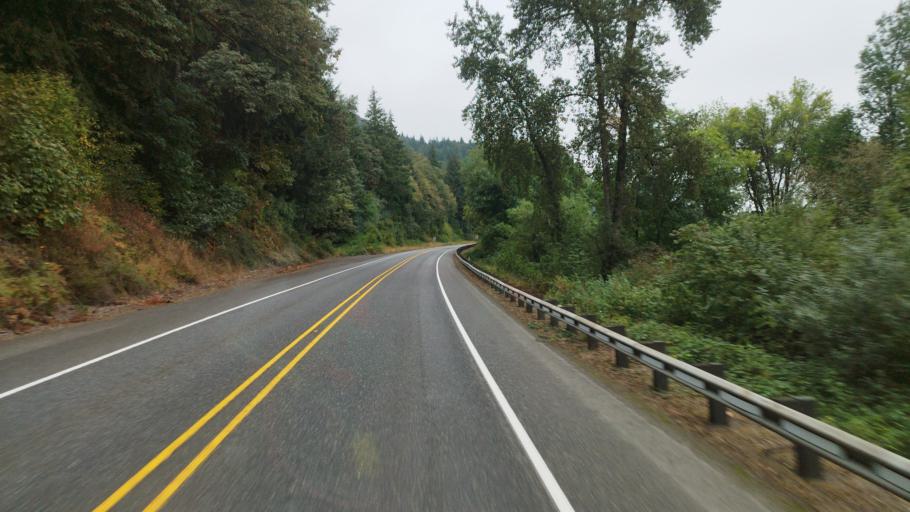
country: US
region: Washington
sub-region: Cowlitz County
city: Kalama
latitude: 46.0389
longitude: -122.8971
